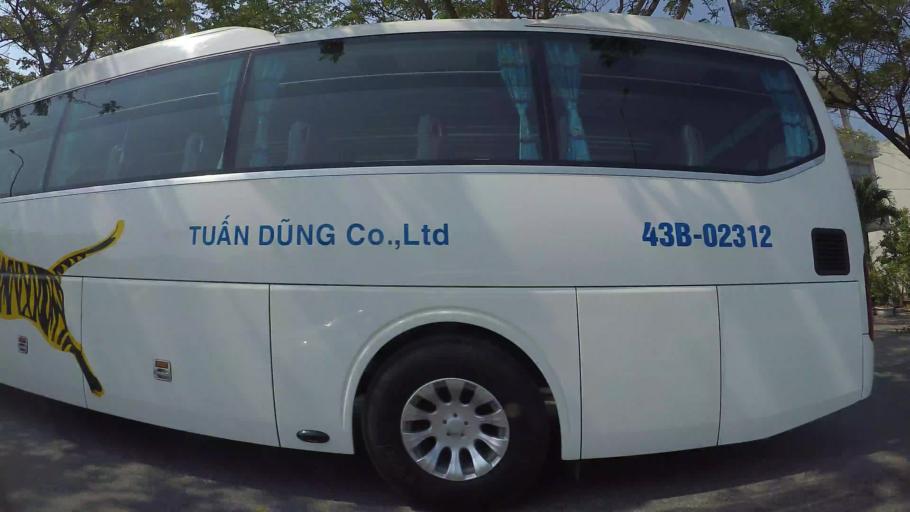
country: VN
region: Da Nang
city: Ngu Hanh Son
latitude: 16.0066
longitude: 108.2604
